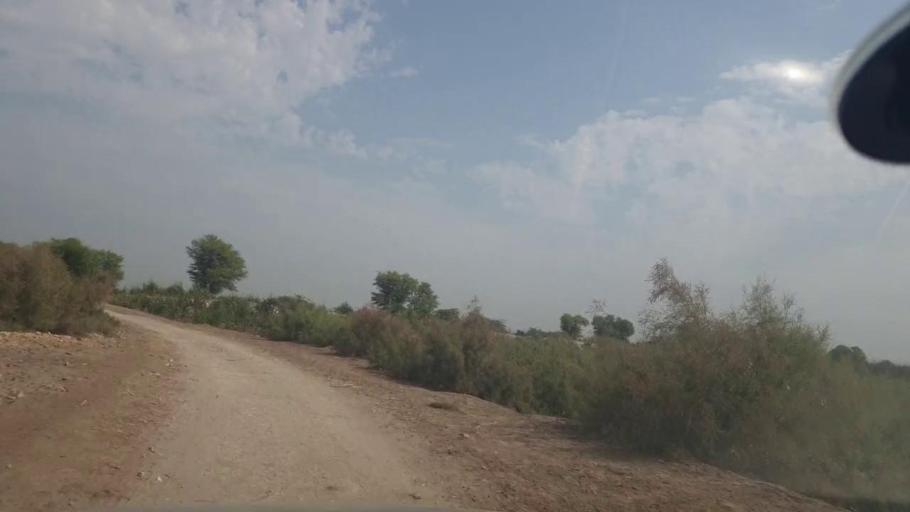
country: PK
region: Balochistan
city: Mehrabpur
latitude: 28.1165
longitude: 68.0913
